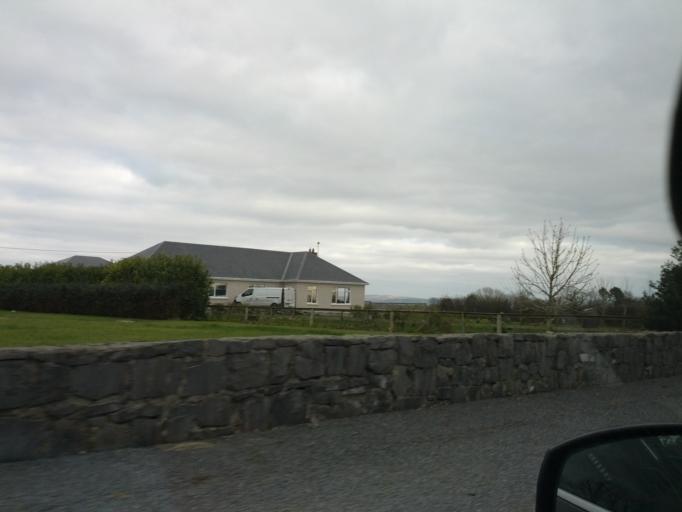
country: IE
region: Connaught
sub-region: County Galway
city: Gort
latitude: 53.1581
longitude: -8.8716
